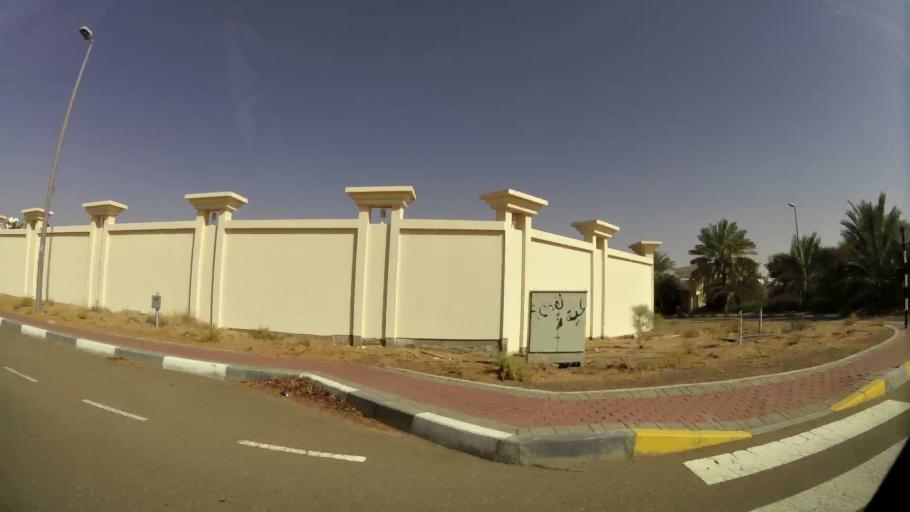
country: OM
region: Al Buraimi
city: Al Buraymi
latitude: 24.3281
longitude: 55.7948
